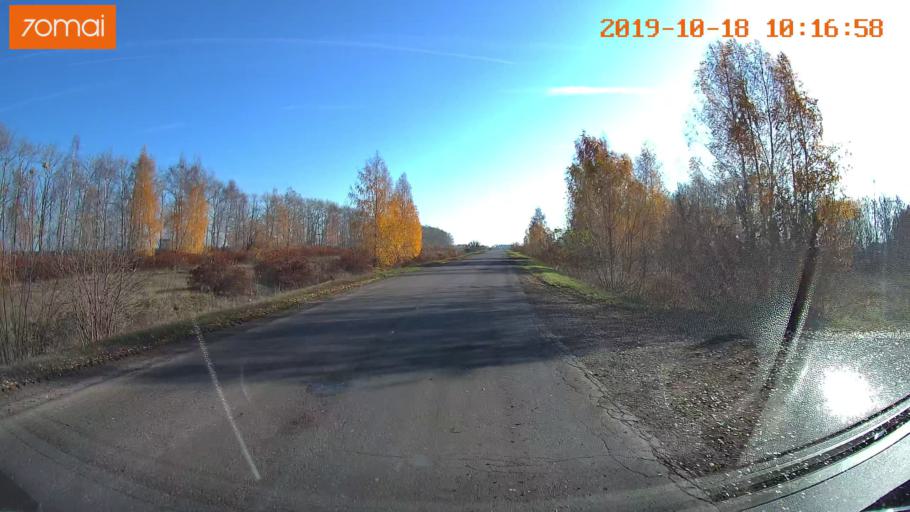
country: RU
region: Tula
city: Kurkino
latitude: 53.4121
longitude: 38.6082
